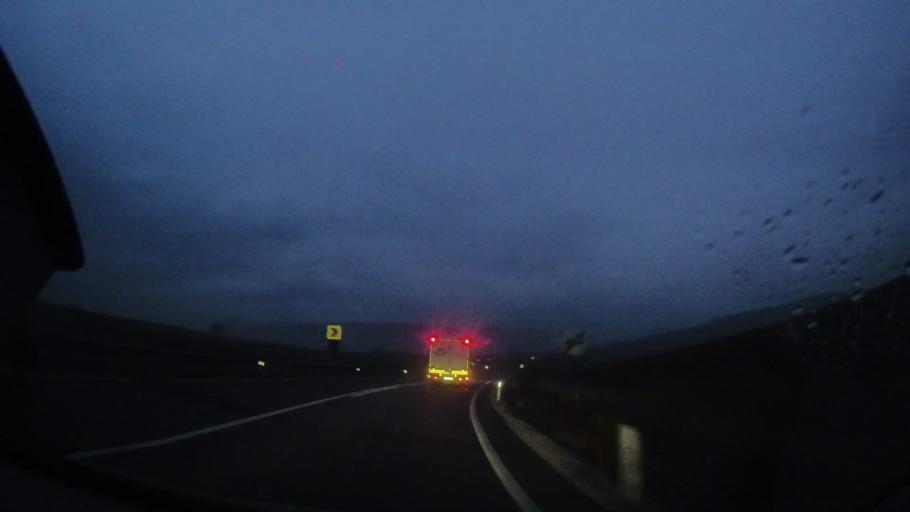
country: RO
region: Harghita
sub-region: Comuna Subcetate
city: Subcetate
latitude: 46.8532
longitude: 25.4685
